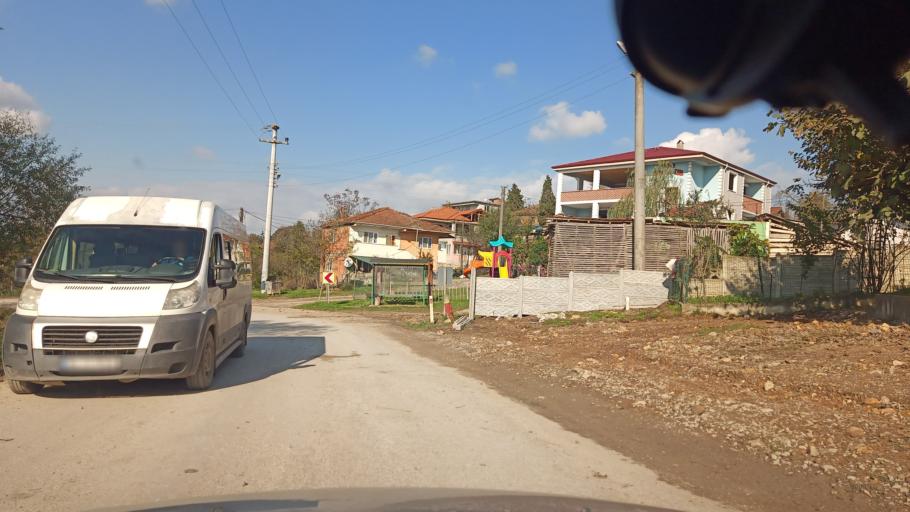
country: TR
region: Sakarya
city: Kaynarca
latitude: 41.0917
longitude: 30.4461
